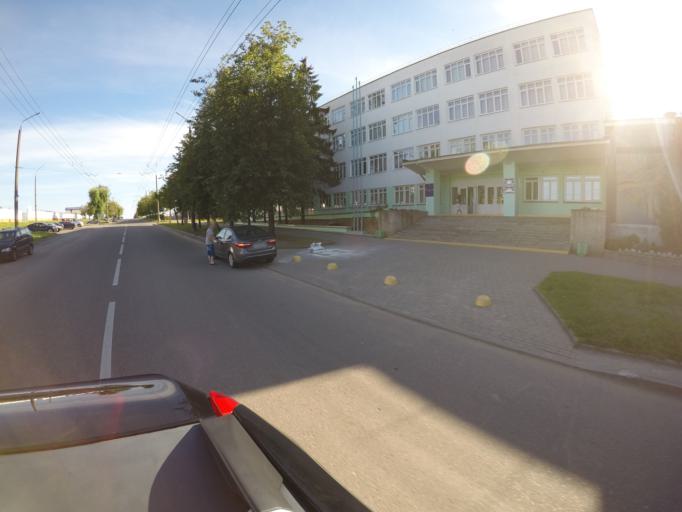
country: BY
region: Grodnenskaya
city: Hrodna
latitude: 53.7122
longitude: 23.8263
